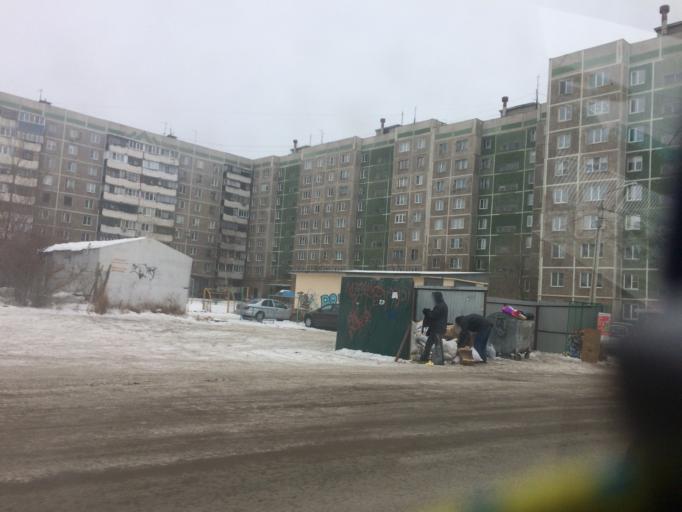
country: RU
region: Chelyabinsk
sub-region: Gorod Magnitogorsk
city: Magnitogorsk
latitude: 53.3600
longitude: 58.9981
